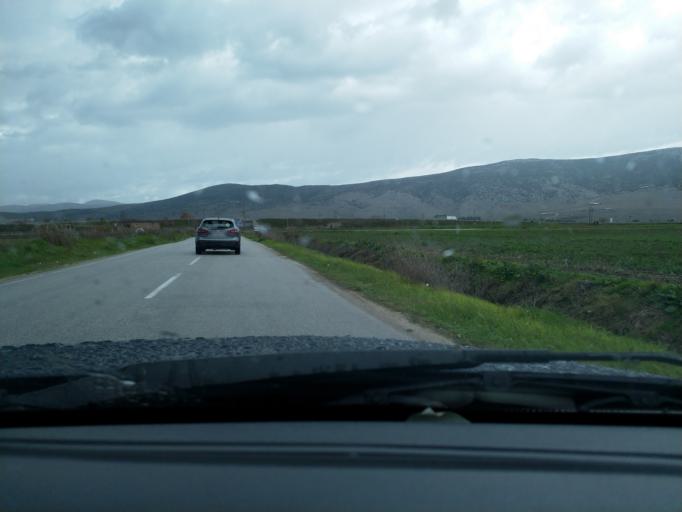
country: GR
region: Thessaly
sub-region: Trikala
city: Taxiarches
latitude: 39.5584
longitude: 21.8900
